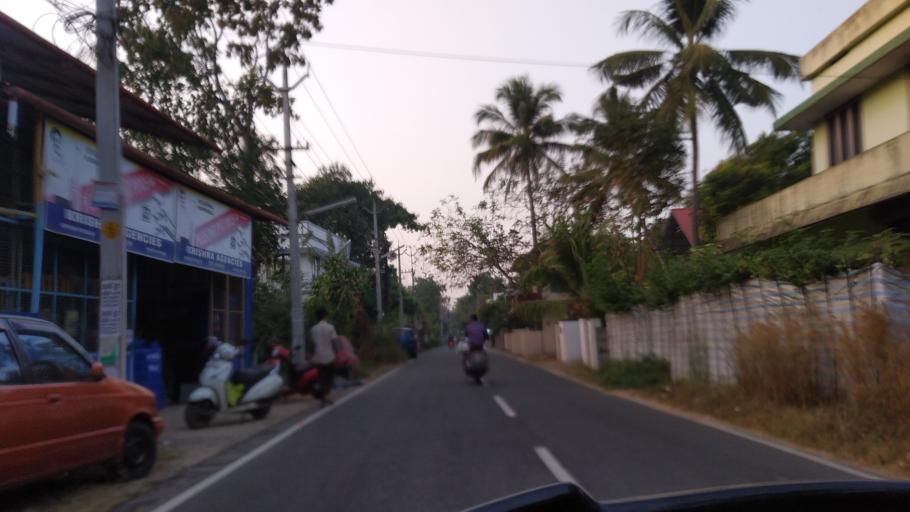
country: IN
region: Kerala
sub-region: Ernakulam
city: Elur
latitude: 10.1269
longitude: 76.2368
